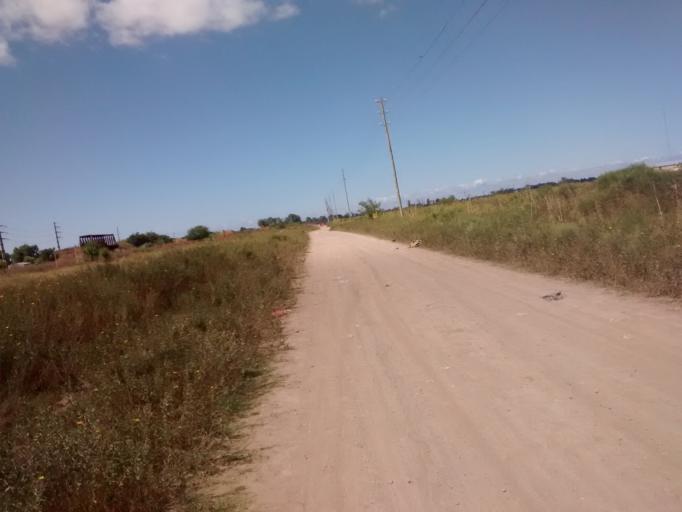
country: AR
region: Buenos Aires
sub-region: Partido de La Plata
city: La Plata
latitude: -34.9675
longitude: -57.9351
